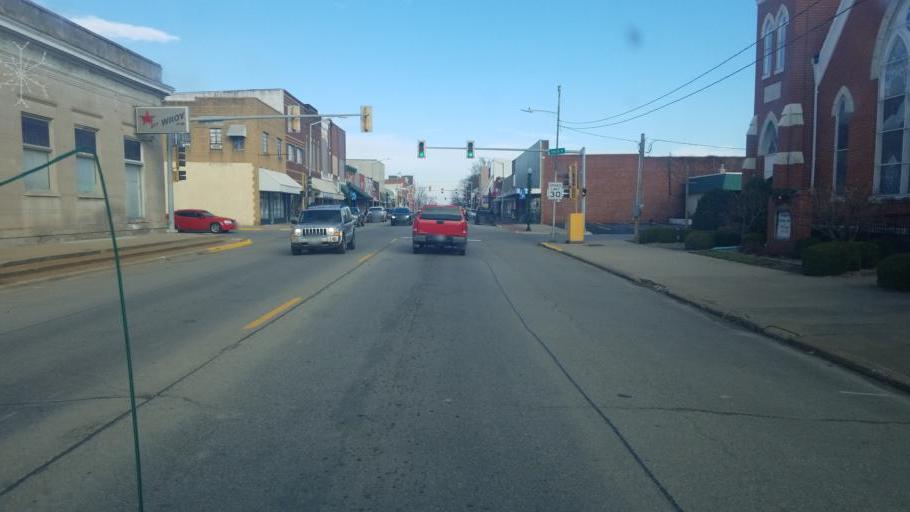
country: US
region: Illinois
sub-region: White County
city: Carmi
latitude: 38.0891
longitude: -88.1616
